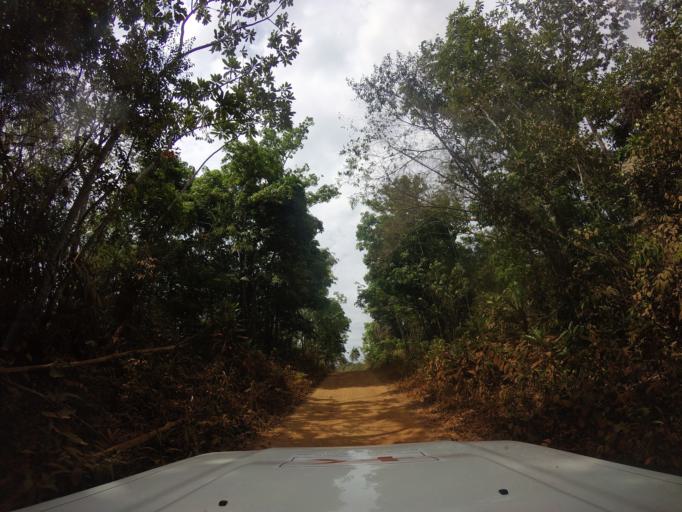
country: LR
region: Grand Cape Mount
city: Robertsport
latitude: 6.9526
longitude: -11.3224
